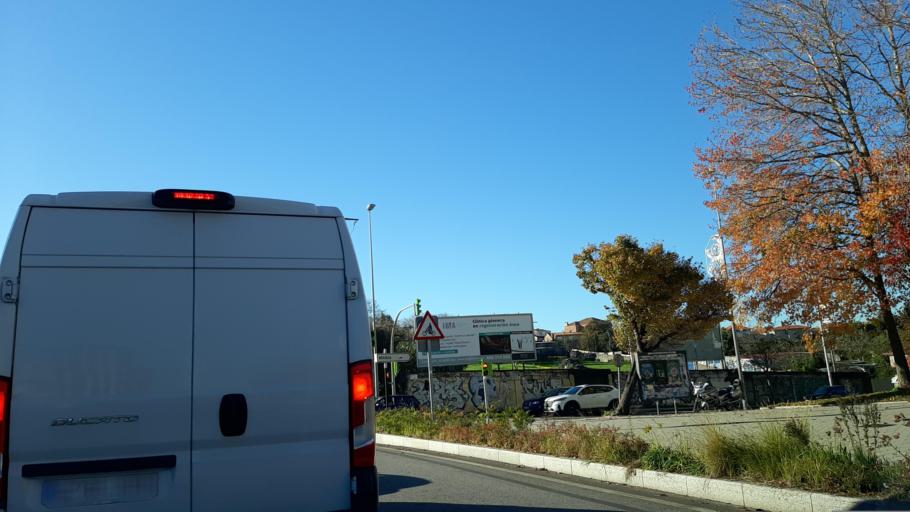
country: ES
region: Galicia
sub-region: Provincia de Pontevedra
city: Vigo
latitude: 42.2172
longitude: -8.7536
